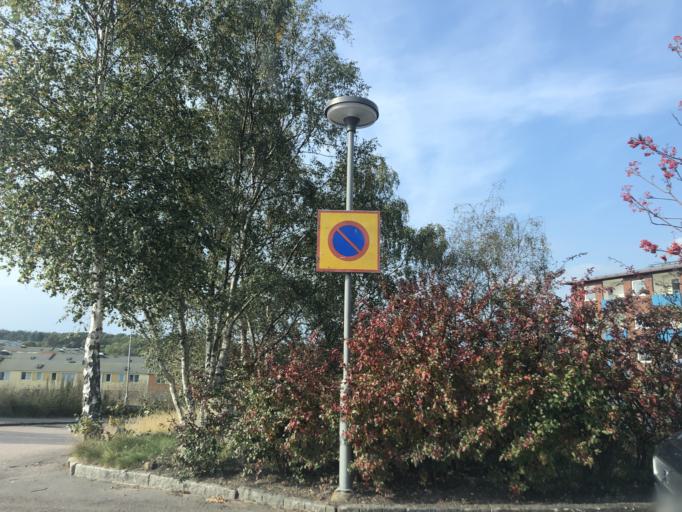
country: SE
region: Vaestra Goetaland
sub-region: Goteborg
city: Majorna
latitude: 57.6450
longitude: 11.9047
